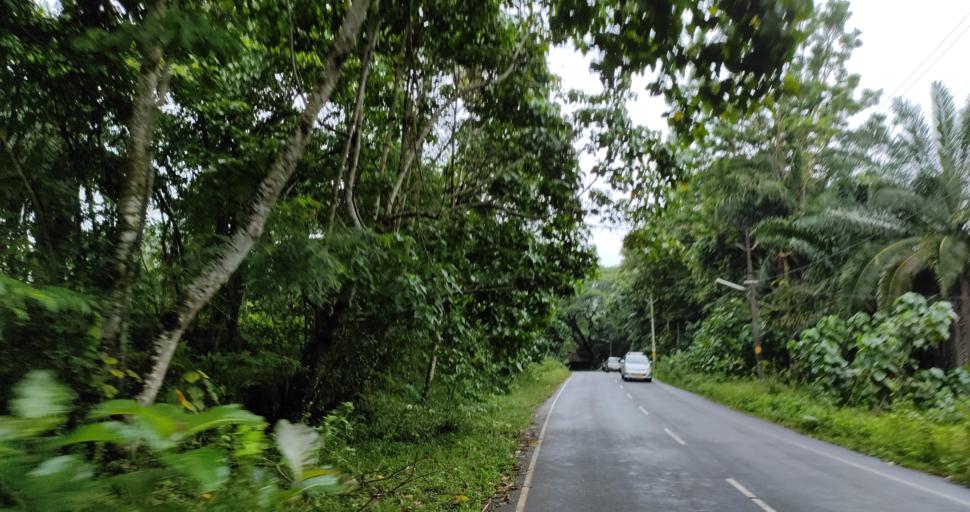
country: IN
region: Kerala
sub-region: Ernakulam
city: Angamali
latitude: 10.2881
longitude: 76.5508
